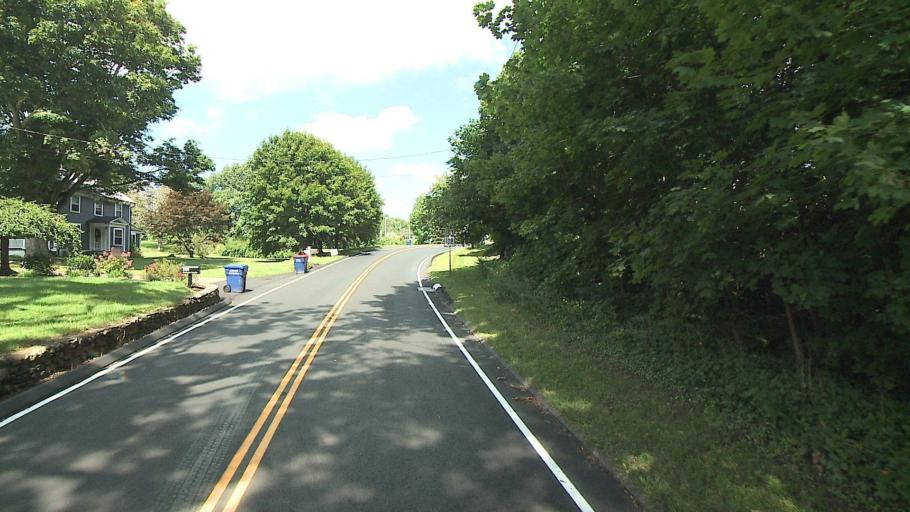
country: US
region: Connecticut
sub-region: Fairfield County
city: Trumbull
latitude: 41.2359
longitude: -73.1617
